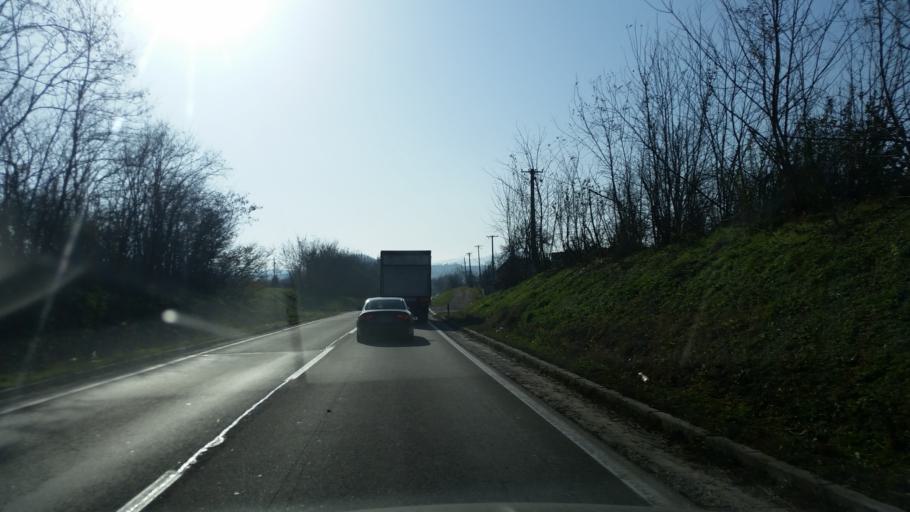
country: RS
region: Central Serbia
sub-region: Kolubarski Okrug
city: Ljig
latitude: 44.2565
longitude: 20.2864
